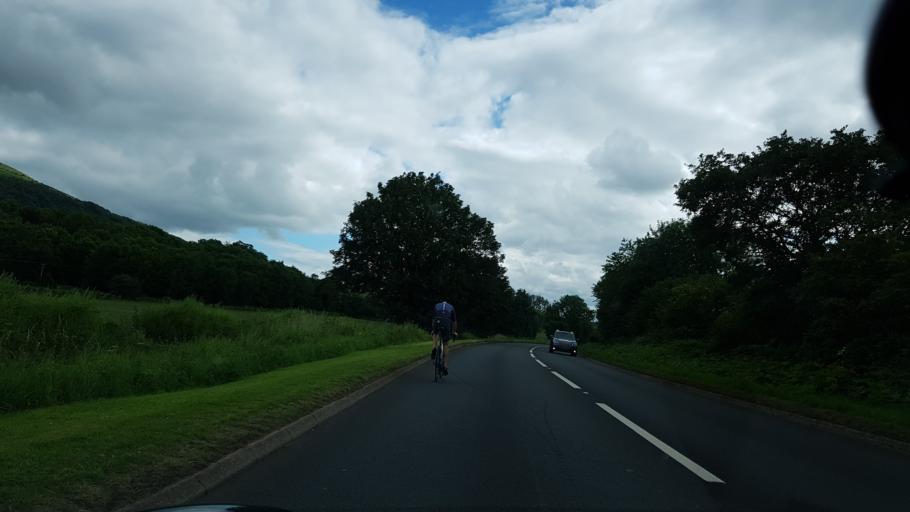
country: GB
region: Wales
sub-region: Monmouthshire
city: Abergavenny
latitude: 51.8689
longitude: -2.9897
